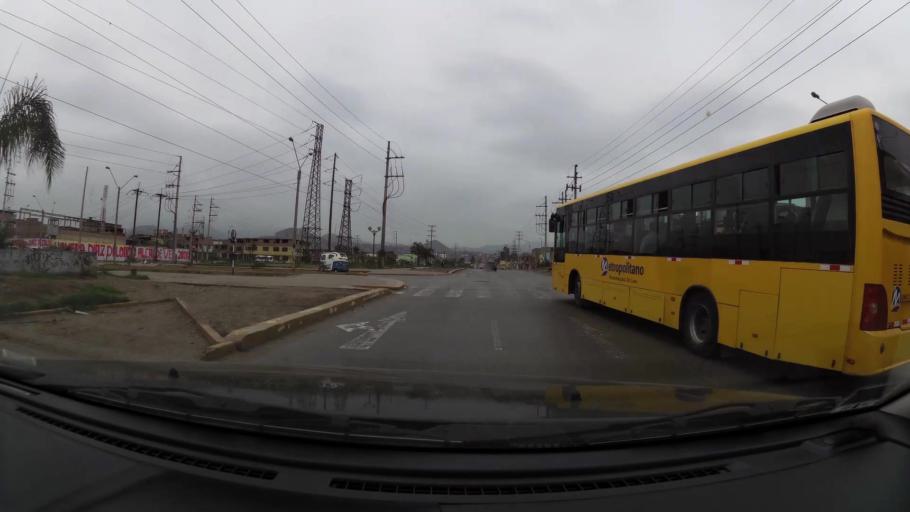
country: PE
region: Lima
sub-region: Lima
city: Surco
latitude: -12.2024
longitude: -76.9469
